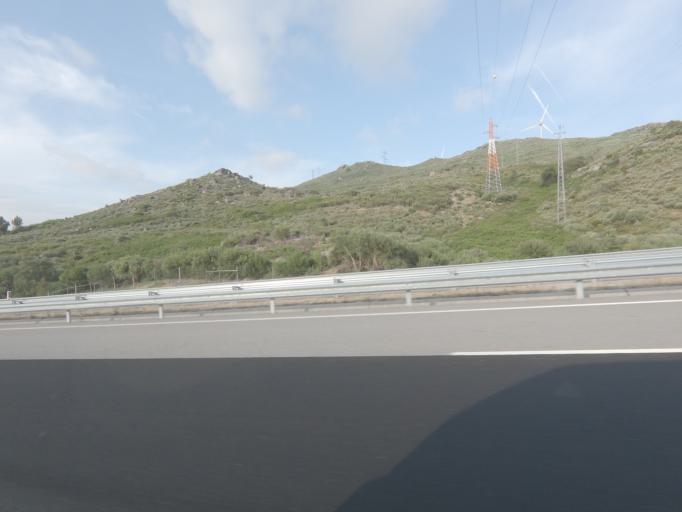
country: PT
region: Vila Real
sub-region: Vila Pouca de Aguiar
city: Vila Pouca de Aguiar
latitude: 41.4650
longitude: -7.6448
